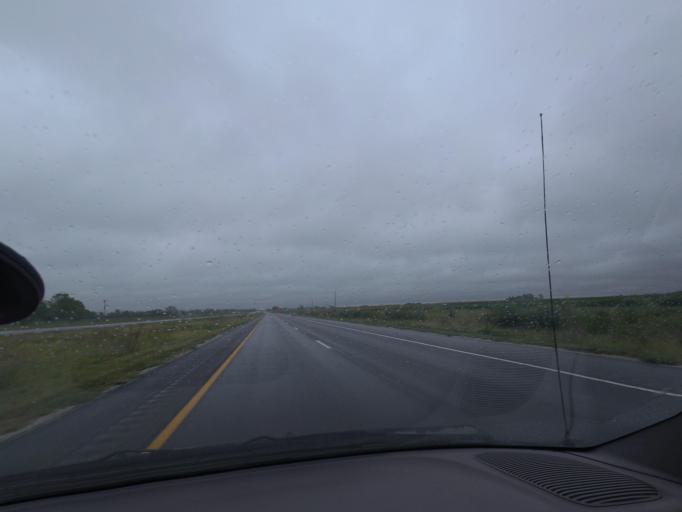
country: US
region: Illinois
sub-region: Scott County
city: Winchester
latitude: 39.6811
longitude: -90.4747
